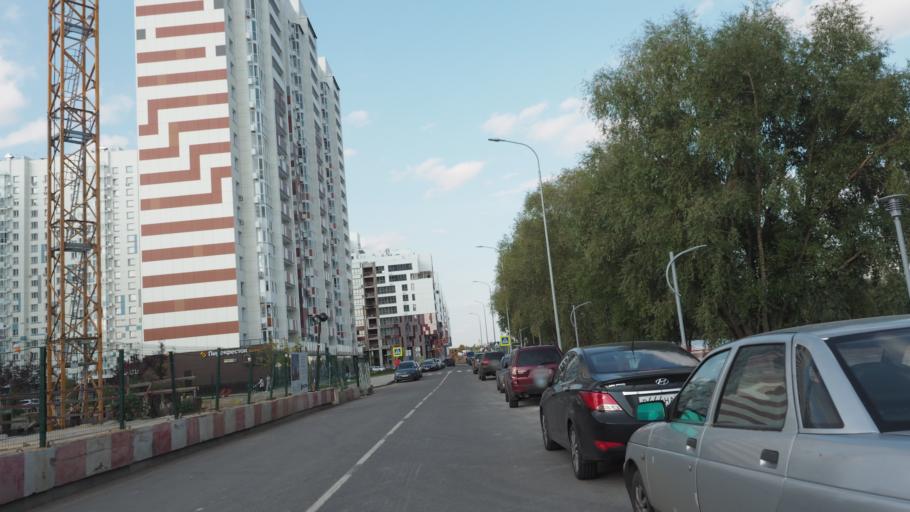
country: RU
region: Moscow
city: Kolomenskoye
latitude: 55.6797
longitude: 37.6960
